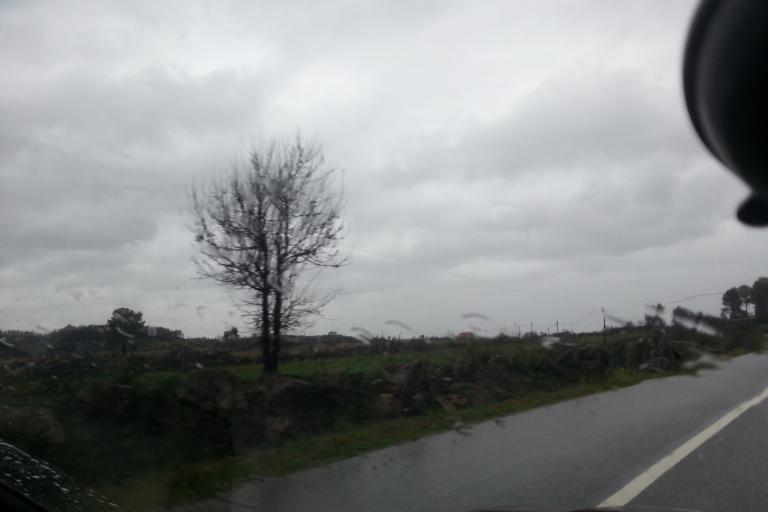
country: PT
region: Guarda
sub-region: Fornos de Algodres
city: Fornos de Algodres
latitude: 40.5613
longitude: -7.5180
